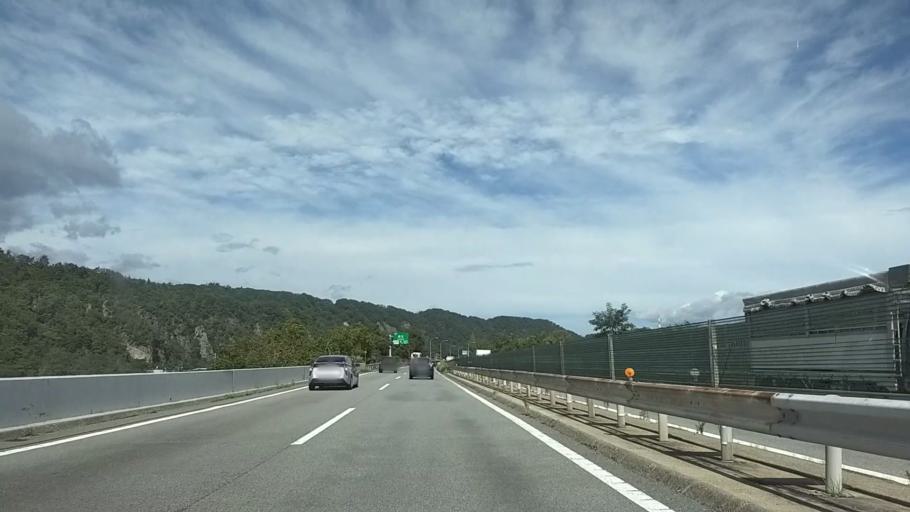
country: JP
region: Yamanashi
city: Nirasaki
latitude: 35.7687
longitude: 138.4283
